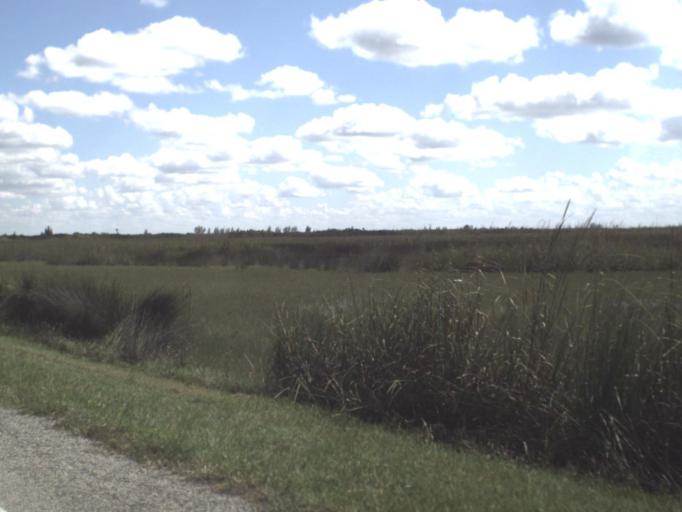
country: US
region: Florida
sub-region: Collier County
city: Marco
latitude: 25.9179
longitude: -81.3855
